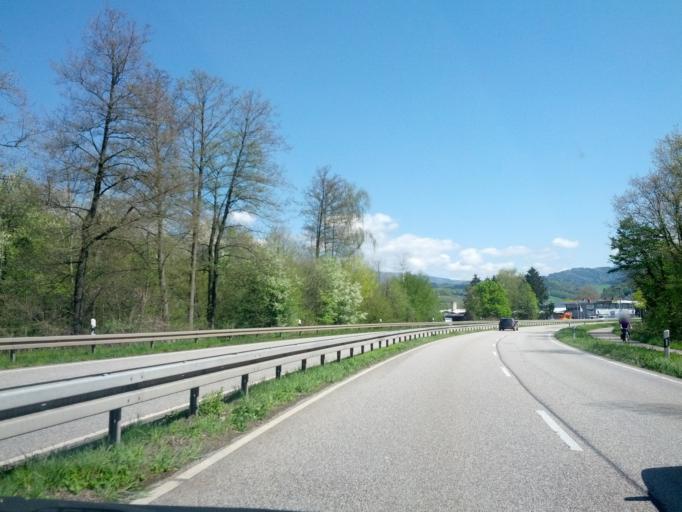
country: DE
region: Baden-Wuerttemberg
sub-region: Freiburg Region
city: Gundelfingen
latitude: 48.0353
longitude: 7.8520
